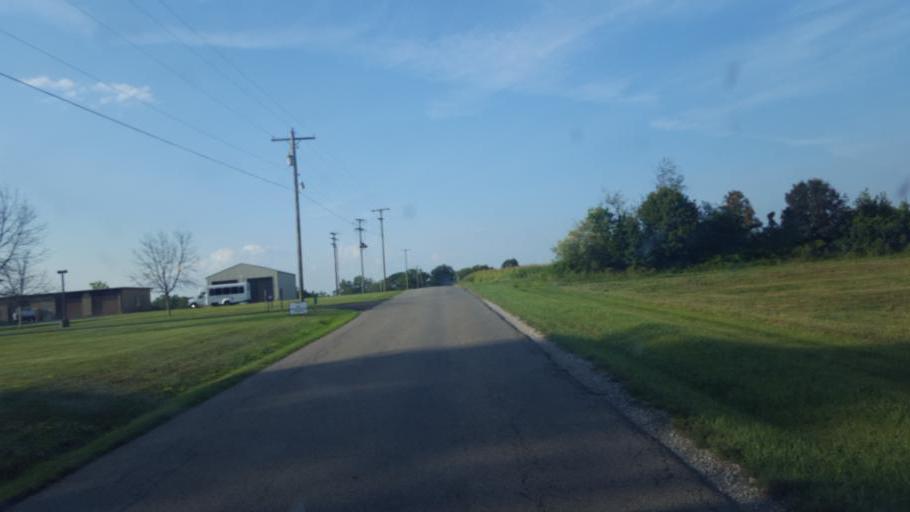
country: US
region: Ohio
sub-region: Knox County
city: Mount Vernon
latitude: 40.3879
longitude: -82.4454
